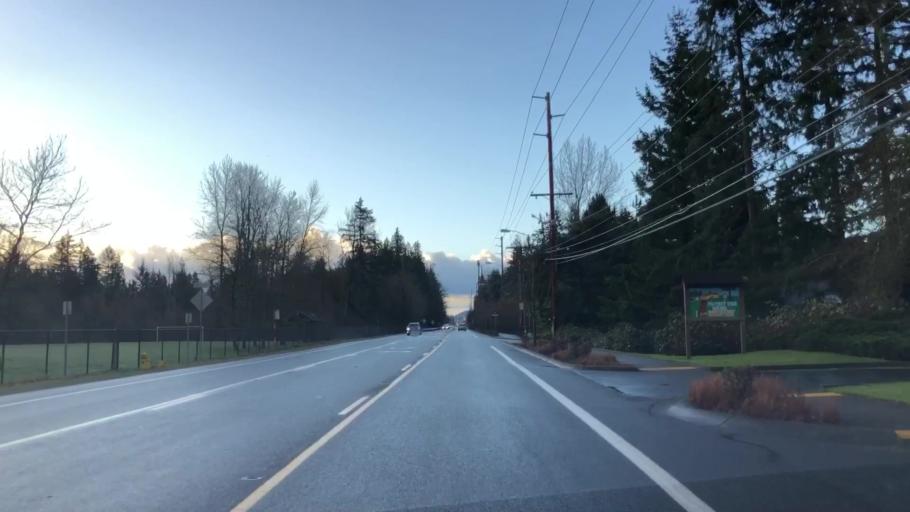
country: US
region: Washington
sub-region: King County
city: City of Sammamish
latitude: 47.6263
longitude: -122.0355
